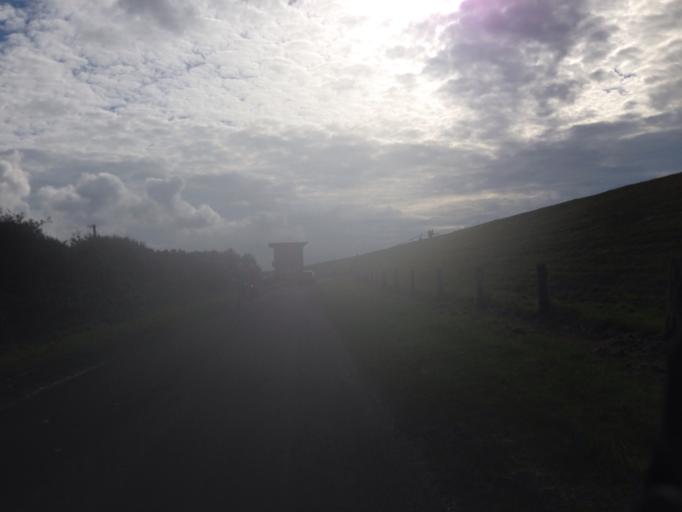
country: DE
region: Schleswig-Holstein
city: Utersum
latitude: 54.7305
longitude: 8.4066
